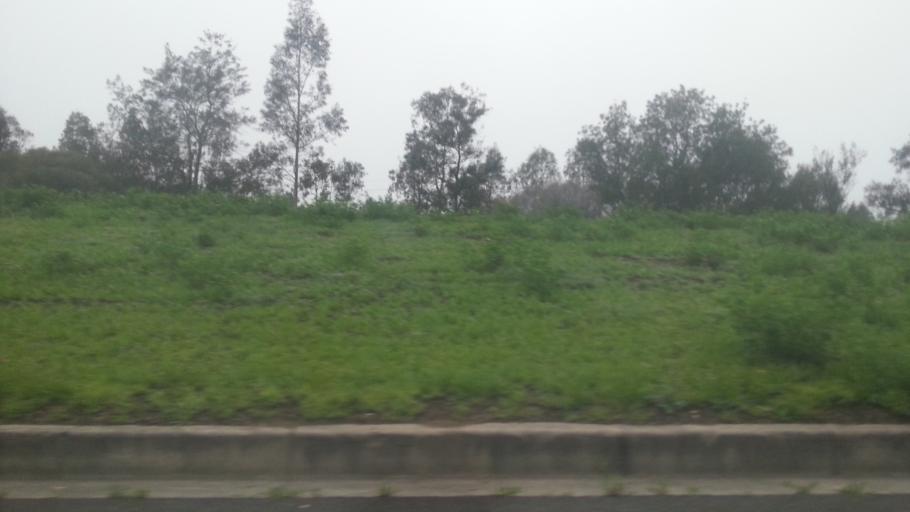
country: AU
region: New South Wales
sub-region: Camden
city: Narellan Vale
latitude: -34.0418
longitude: 150.7445
